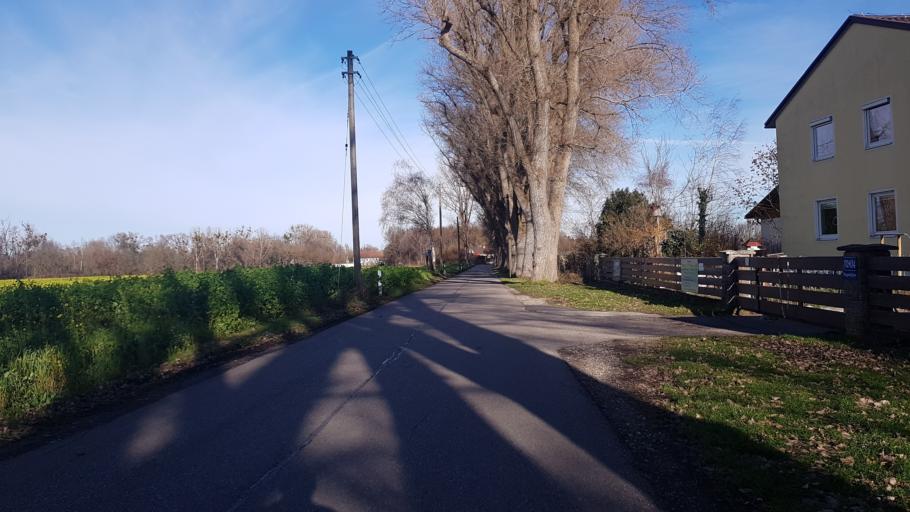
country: DE
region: Bavaria
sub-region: Upper Bavaria
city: Karlsfeld
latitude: 48.2098
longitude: 11.5186
